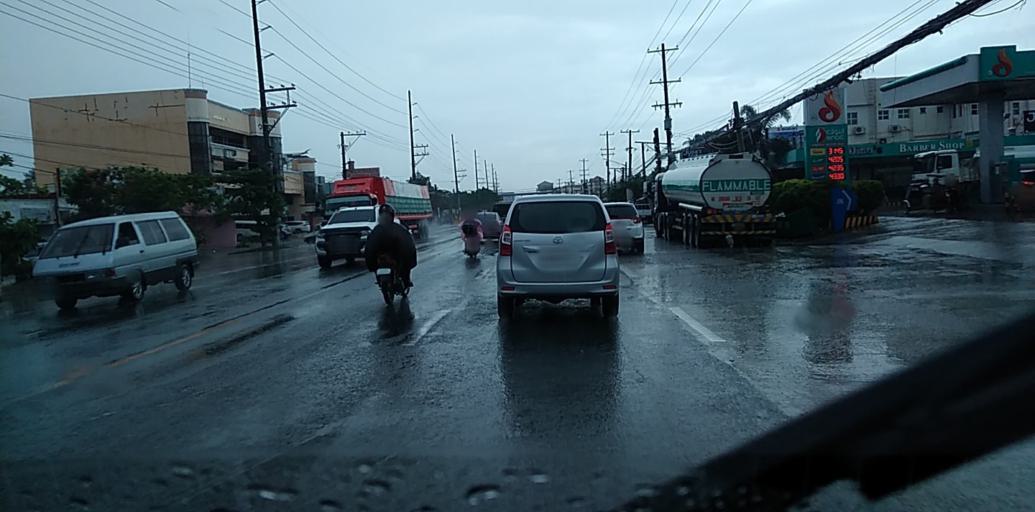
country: PH
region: Central Luzon
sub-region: Province of Pampanga
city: Magliman
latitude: 15.0553
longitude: 120.6602
